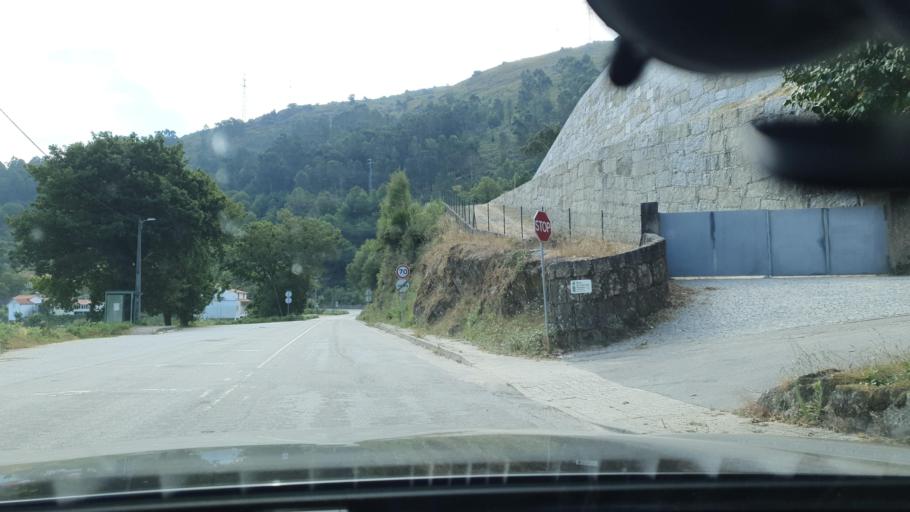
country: PT
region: Braga
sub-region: Vieira do Minho
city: Vieira do Minho
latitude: 41.6783
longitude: -8.1230
